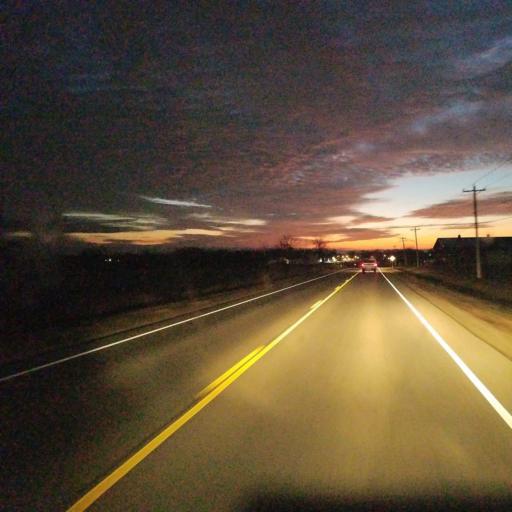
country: US
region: Illinois
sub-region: Peoria County
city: Hanna City
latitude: 40.6950
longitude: -89.8095
